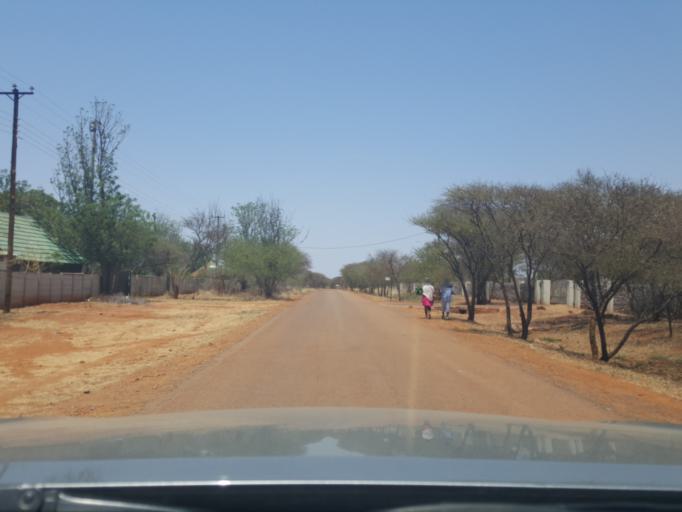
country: BW
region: South East
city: Ramotswa
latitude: -24.7714
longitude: 25.8452
